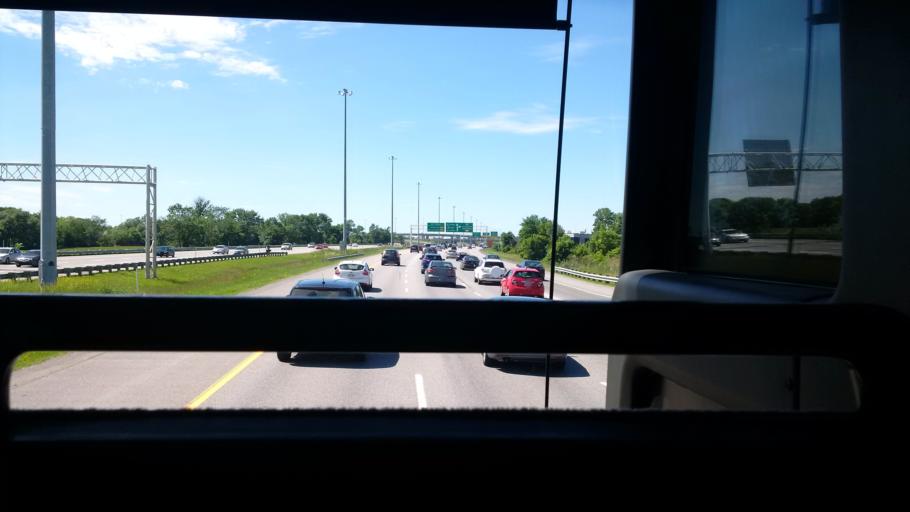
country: CA
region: Quebec
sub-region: Laurentides
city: Boisbriand
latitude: 45.6204
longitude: -73.8296
